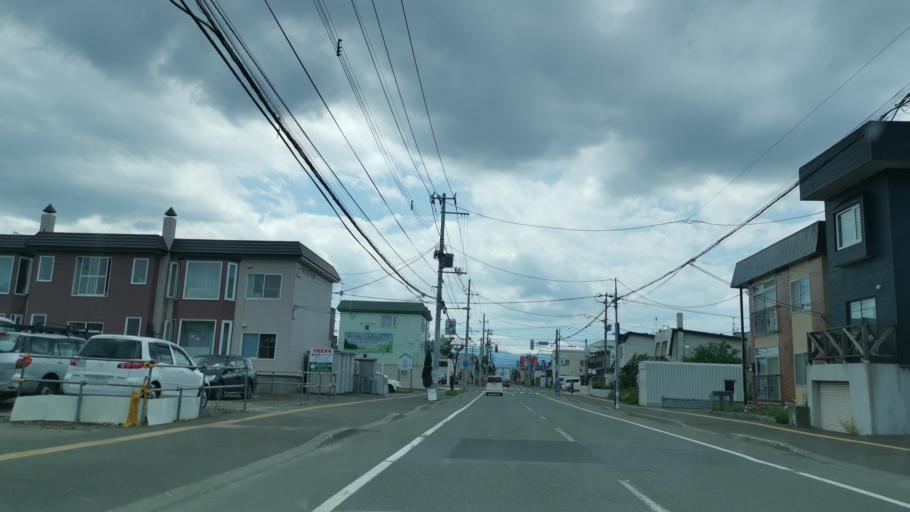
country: JP
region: Hokkaido
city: Sapporo
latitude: 43.0704
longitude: 141.4136
